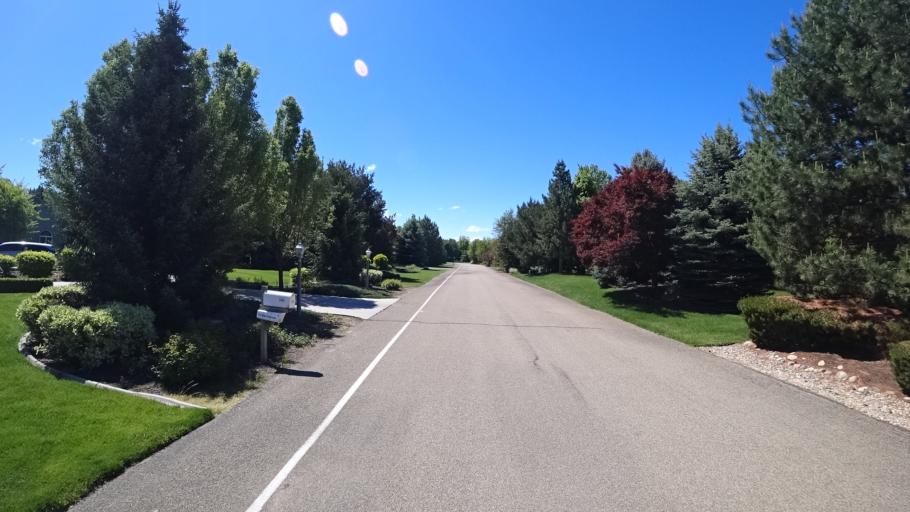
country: US
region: Idaho
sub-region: Ada County
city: Eagle
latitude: 43.6688
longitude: -116.3914
